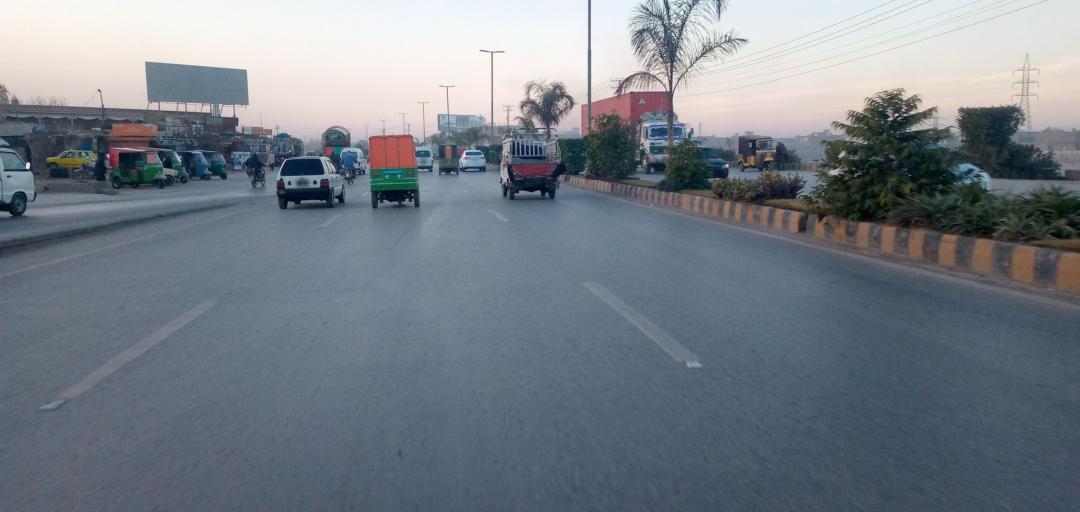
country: PK
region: Khyber Pakhtunkhwa
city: Peshawar
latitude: 34.0270
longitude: 71.6175
